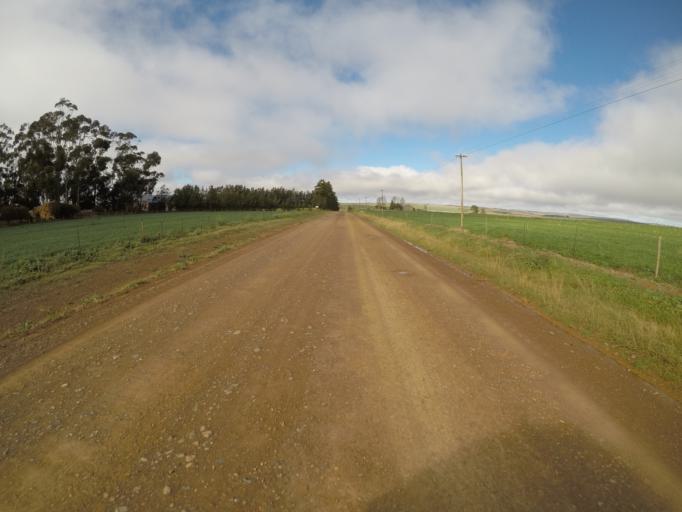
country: ZA
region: Western Cape
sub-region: Cape Winelands District Municipality
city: Ashton
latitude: -34.1405
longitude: 19.8626
